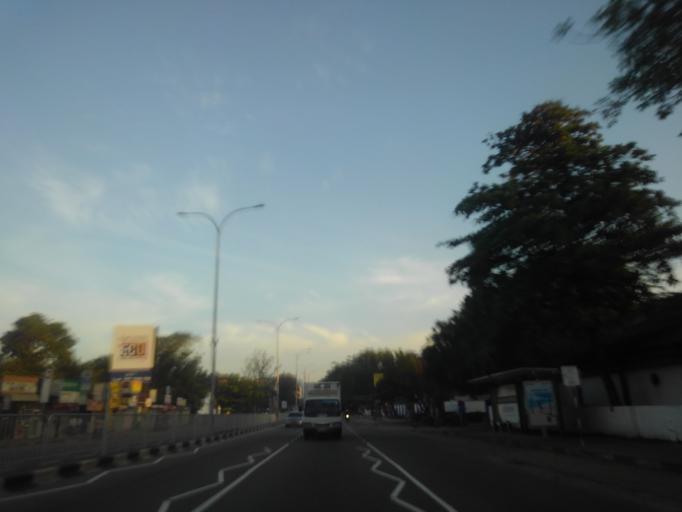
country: LK
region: Western
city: Pita Kotte
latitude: 6.8985
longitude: 79.8772
